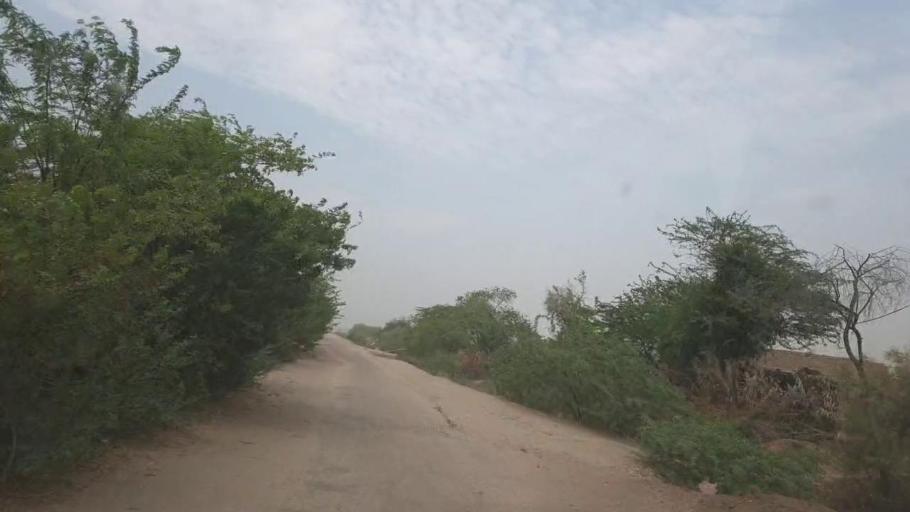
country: PK
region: Sindh
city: Kot Diji
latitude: 27.4407
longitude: 68.7146
